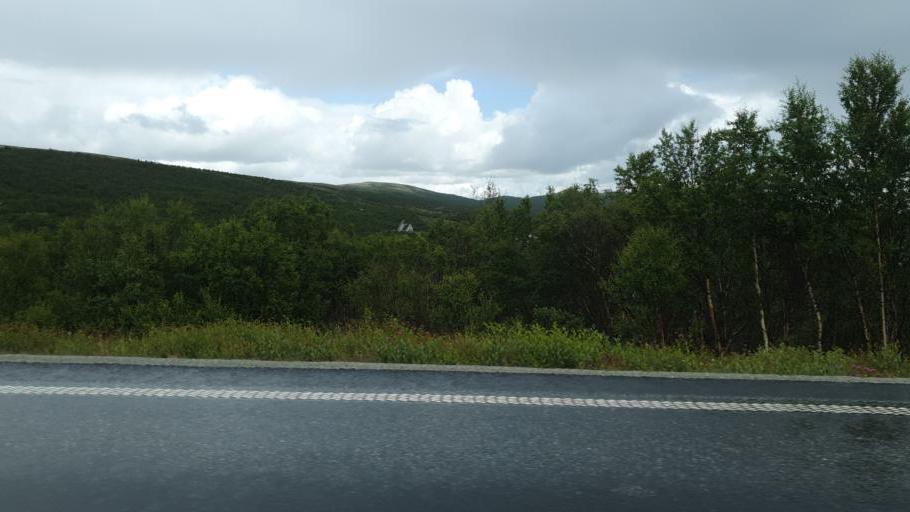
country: NO
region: Oppland
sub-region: Dovre
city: Dovre
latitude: 62.2194
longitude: 9.5514
